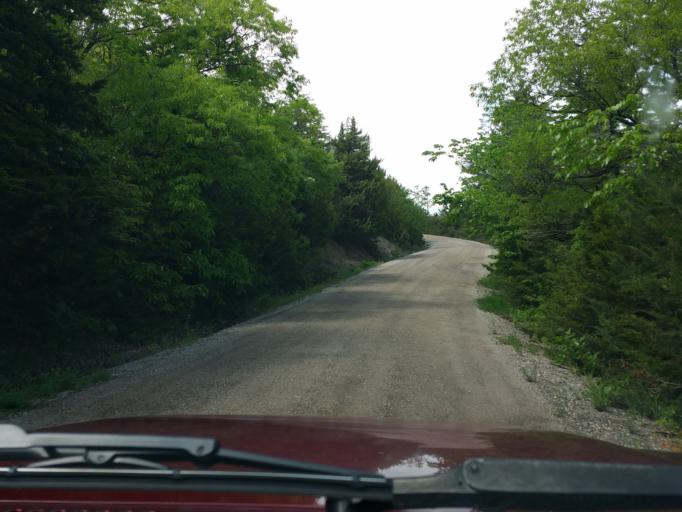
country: US
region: Kansas
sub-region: Riley County
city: Manhattan
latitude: 39.2963
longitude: -96.6500
